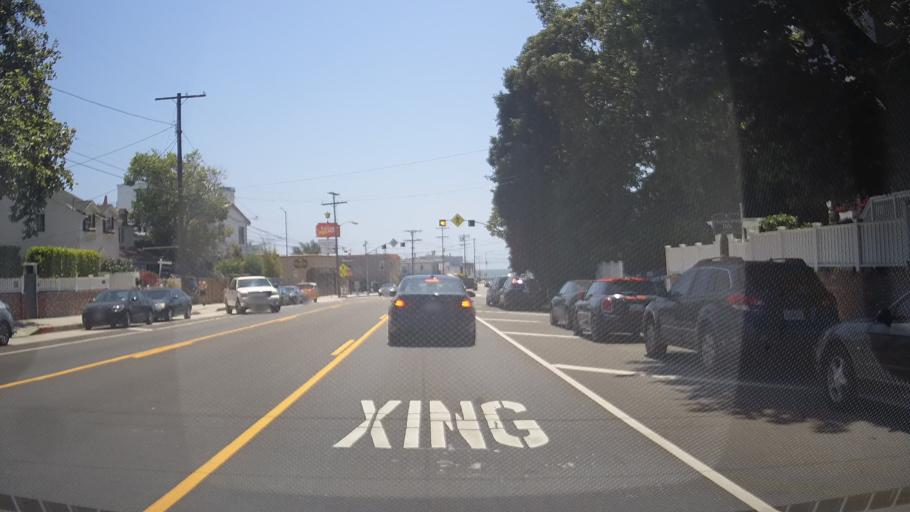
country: US
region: California
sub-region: Los Angeles County
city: Santa Monica
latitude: 34.0298
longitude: -118.5172
